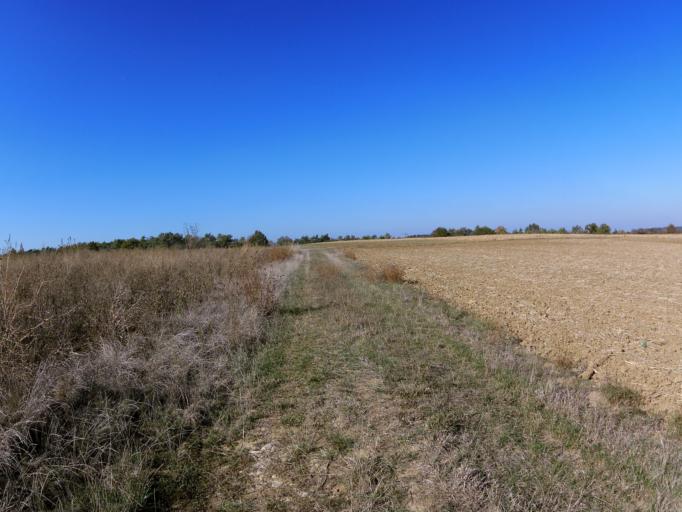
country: DE
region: Bavaria
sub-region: Regierungsbezirk Unterfranken
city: Eibelstadt
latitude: 49.7138
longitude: 9.9884
